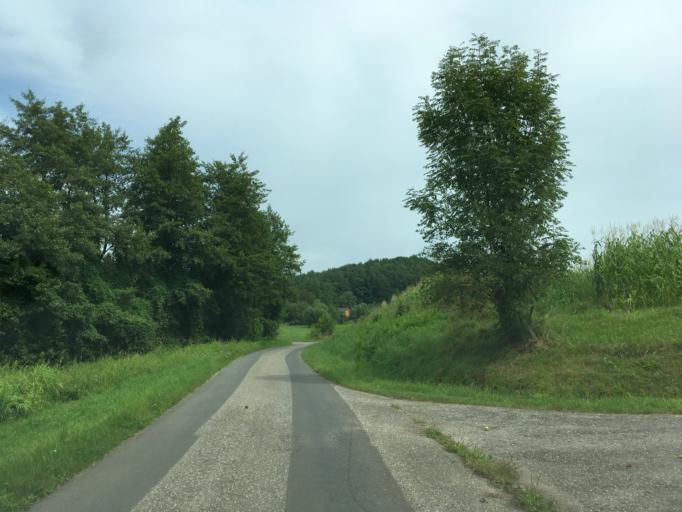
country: AT
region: Styria
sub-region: Politischer Bezirk Deutschlandsberg
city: Wettmannstatten
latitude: 46.7941
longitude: 15.4029
